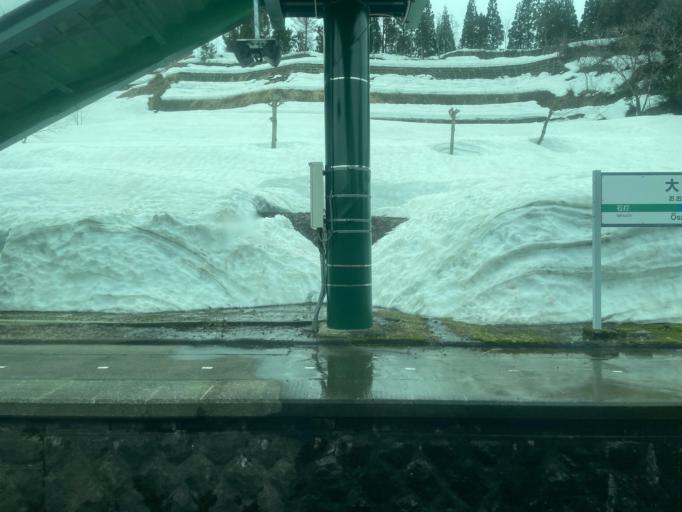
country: JP
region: Niigata
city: Shiozawa
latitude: 37.0215
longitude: 138.8213
